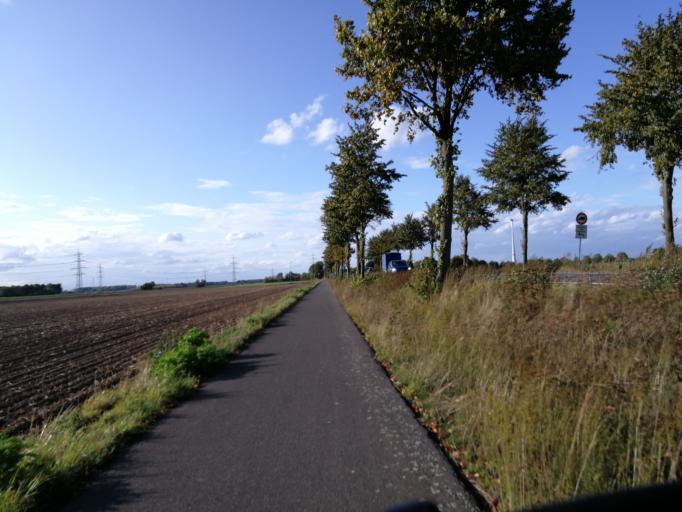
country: DE
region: North Rhine-Westphalia
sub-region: Regierungsbezirk Dusseldorf
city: Neubrueck
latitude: 51.1191
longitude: 6.7077
